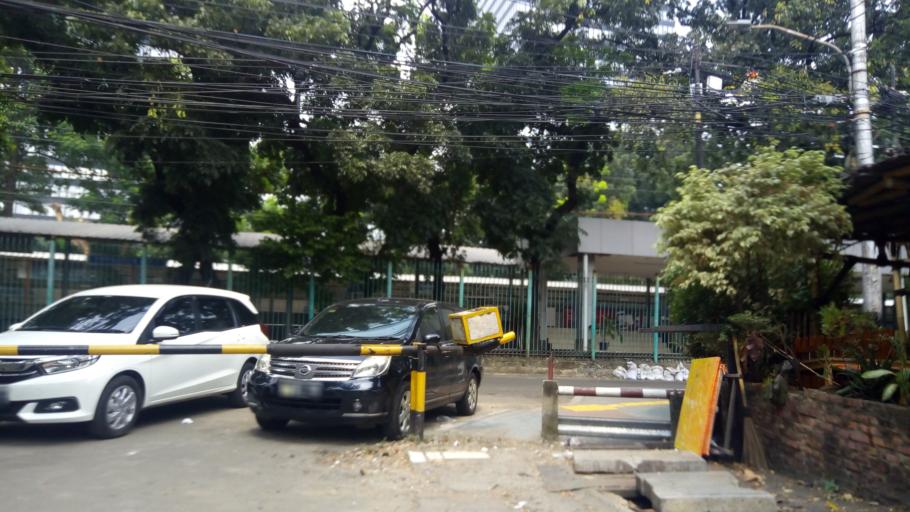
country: ID
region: Jakarta Raya
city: Jakarta
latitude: -6.2023
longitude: 106.8248
